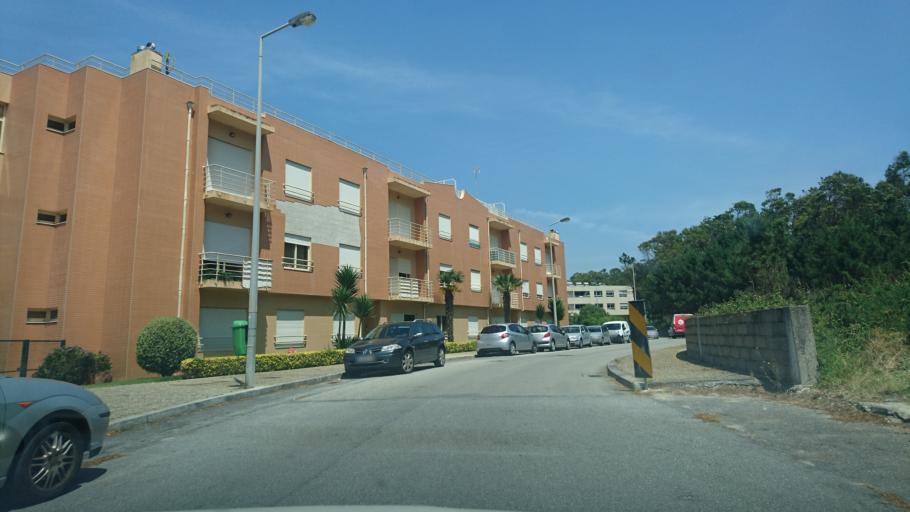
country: PT
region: Porto
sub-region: Matosinhos
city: Lavra
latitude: 41.2723
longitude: -8.7231
